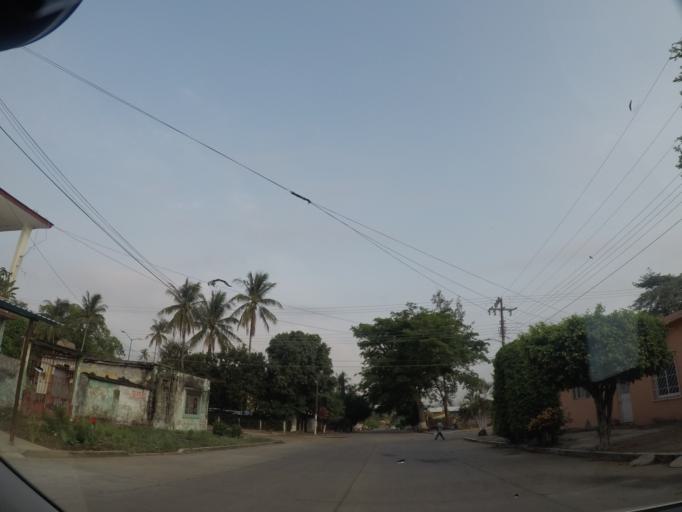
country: MX
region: Oaxaca
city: Matias Romero
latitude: 16.8737
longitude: -95.0420
